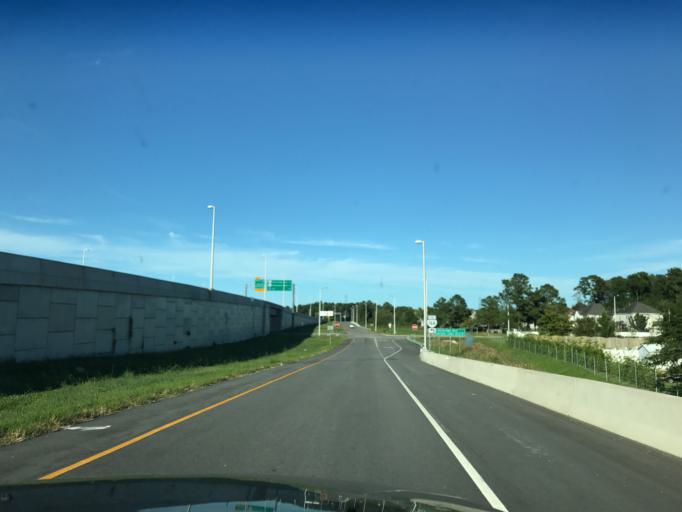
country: US
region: Virginia
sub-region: City of Chesapeake
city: Chesapeake
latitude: 36.7461
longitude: -76.2854
